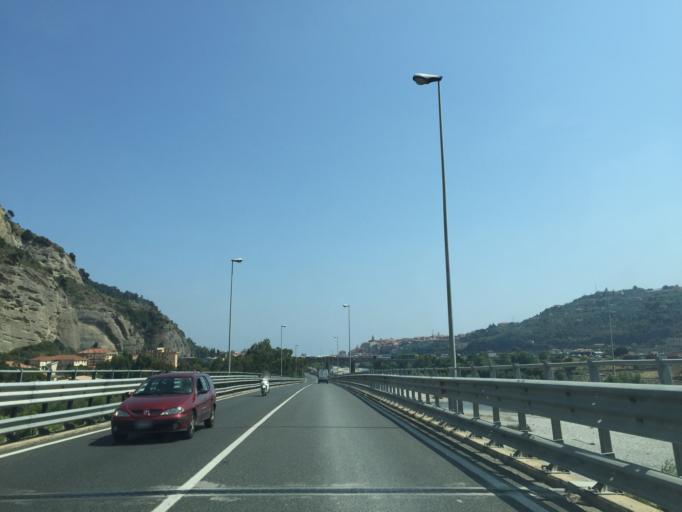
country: IT
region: Liguria
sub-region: Provincia di Imperia
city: Ventimiglia
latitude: 43.8054
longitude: 7.5942
